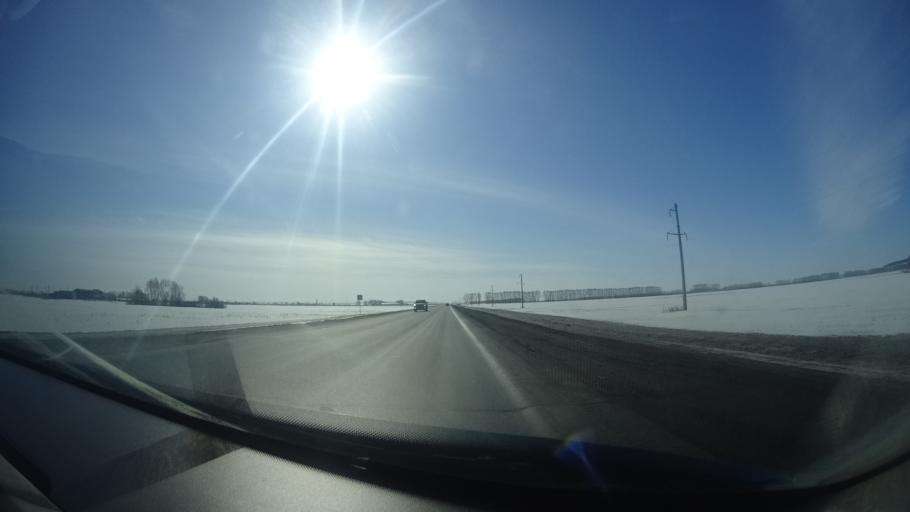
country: RU
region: Bashkortostan
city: Mikhaylovka
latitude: 54.9674
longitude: 55.7633
